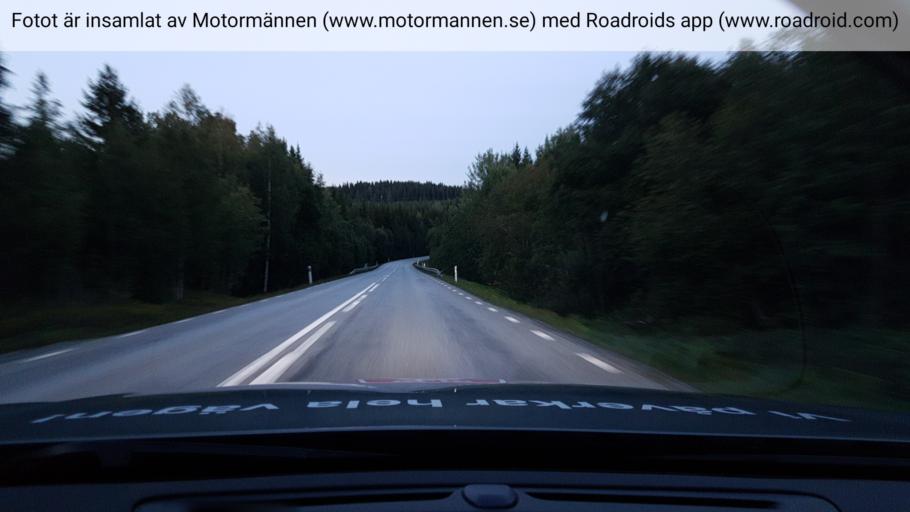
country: SE
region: OErebro
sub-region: Ljusnarsbergs Kommun
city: Kopparberg
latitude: 59.8692
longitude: 15.0297
